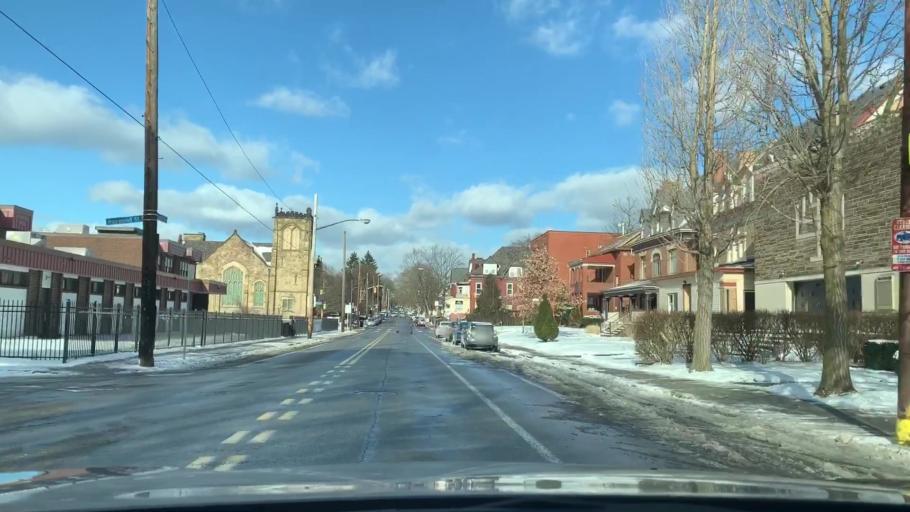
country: US
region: Pennsylvania
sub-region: Allegheny County
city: Sharpsburg
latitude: 40.4706
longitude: -79.9267
